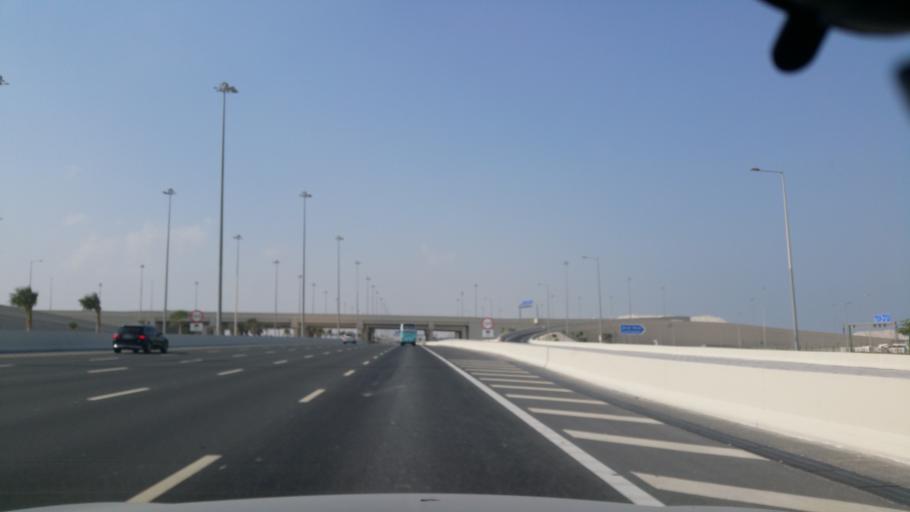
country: QA
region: Baladiyat Umm Salal
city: Umm Salal Muhammad
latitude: 25.4270
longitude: 51.4854
